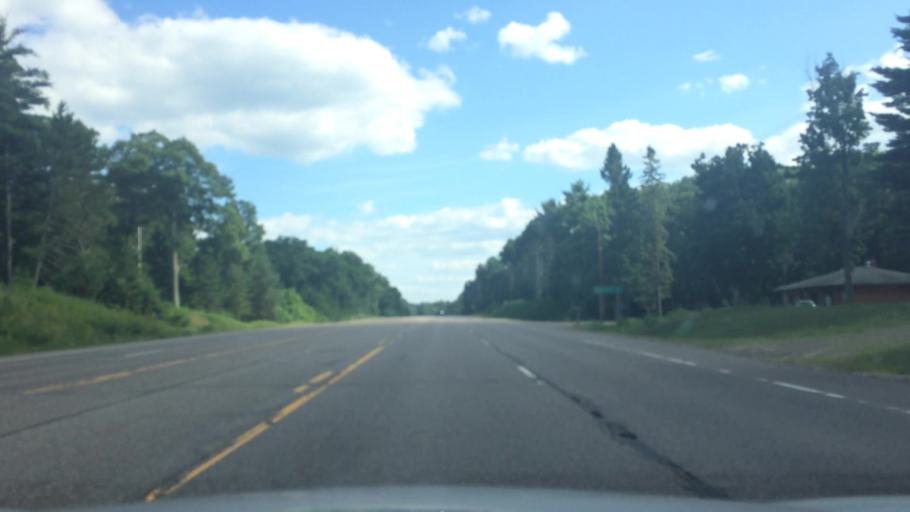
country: US
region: Wisconsin
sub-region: Vilas County
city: Lac du Flambeau
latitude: 45.8153
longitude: -89.7267
